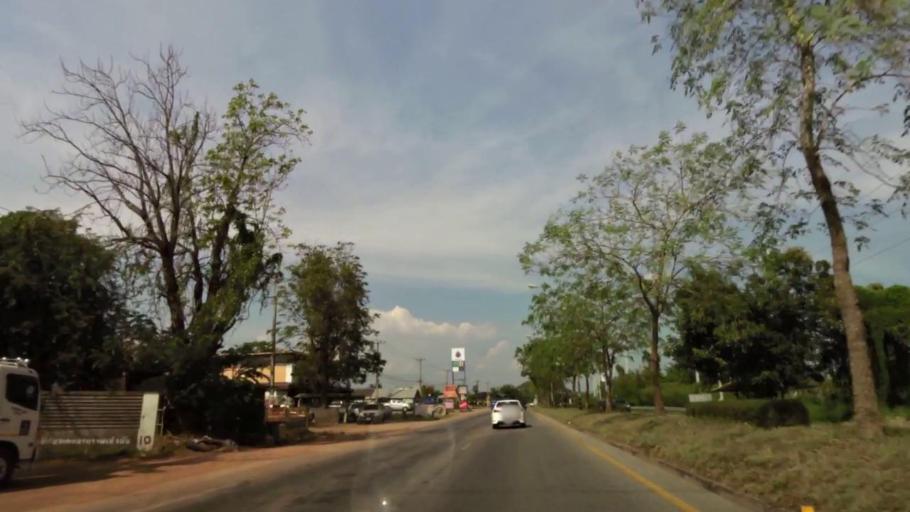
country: TH
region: Uttaradit
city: Uttaradit
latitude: 17.5959
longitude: 100.1284
